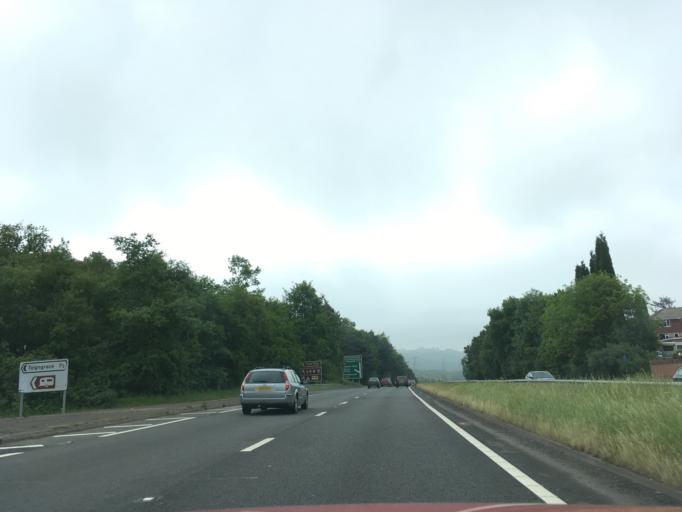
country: GB
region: England
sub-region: Devon
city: Bovey Tracey
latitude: 50.5706
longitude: -3.6470
